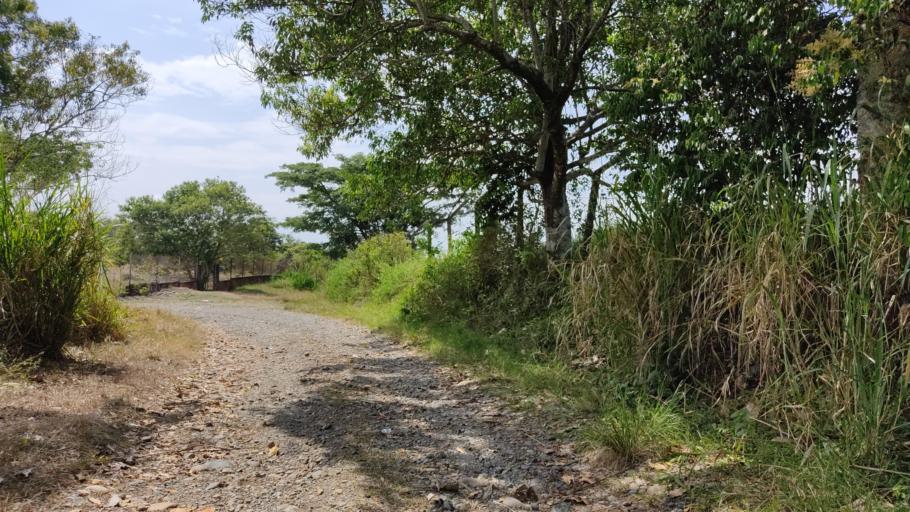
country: CO
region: Cauca
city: Buenos Aires
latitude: 3.1356
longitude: -76.5901
